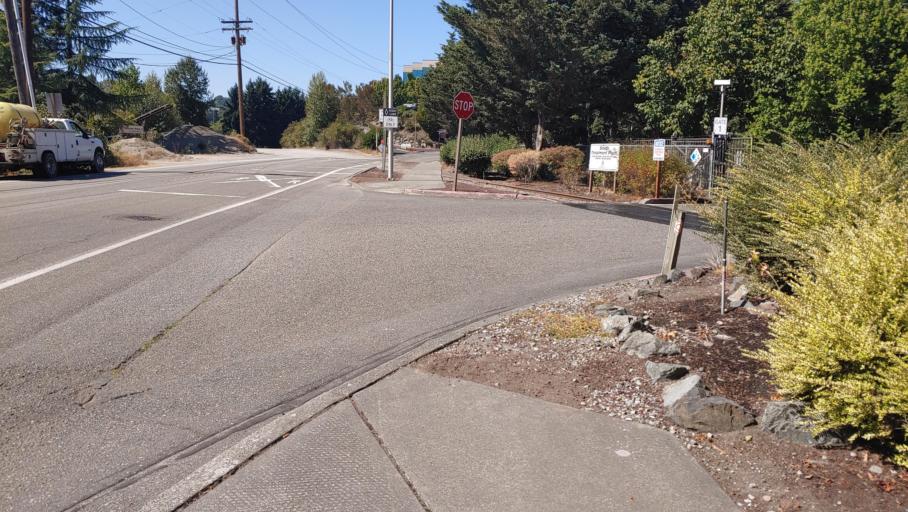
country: US
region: Washington
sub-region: King County
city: Tukwila
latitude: 47.4686
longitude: -122.2428
